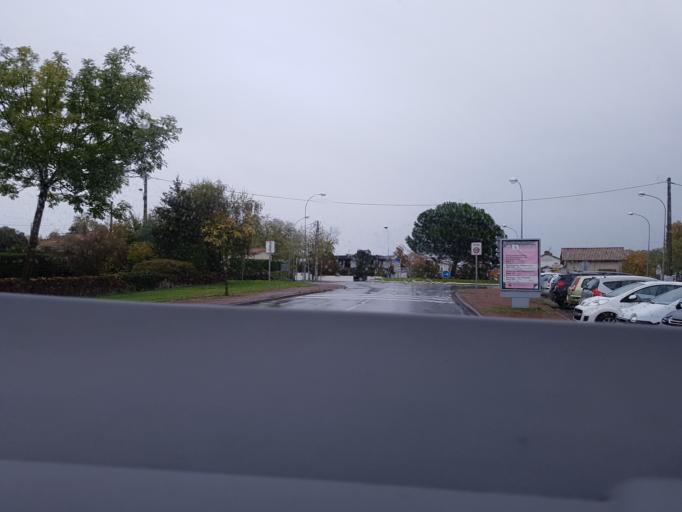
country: FR
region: Aquitaine
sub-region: Departement de la Gironde
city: Cubzac-les-Ponts
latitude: 44.9909
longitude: -0.4432
